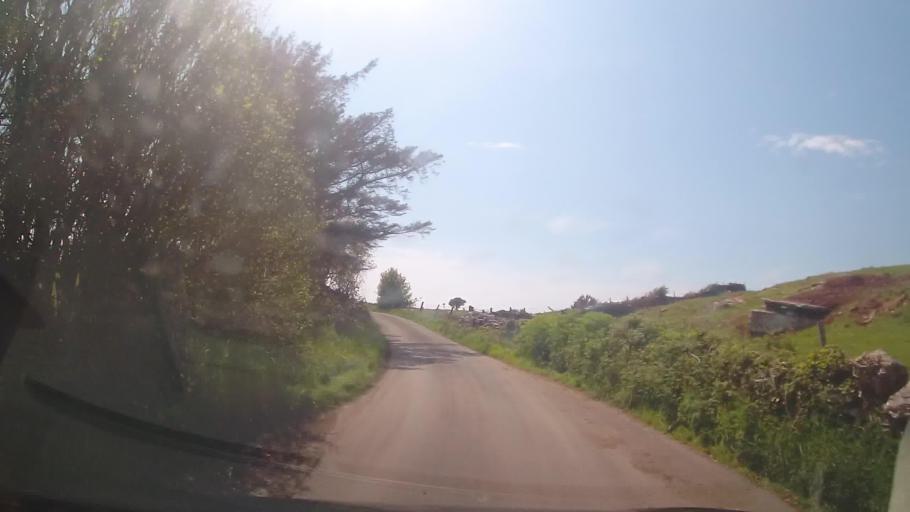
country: GB
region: Wales
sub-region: Gwynedd
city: Porthmadog
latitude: 52.9220
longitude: -4.1790
